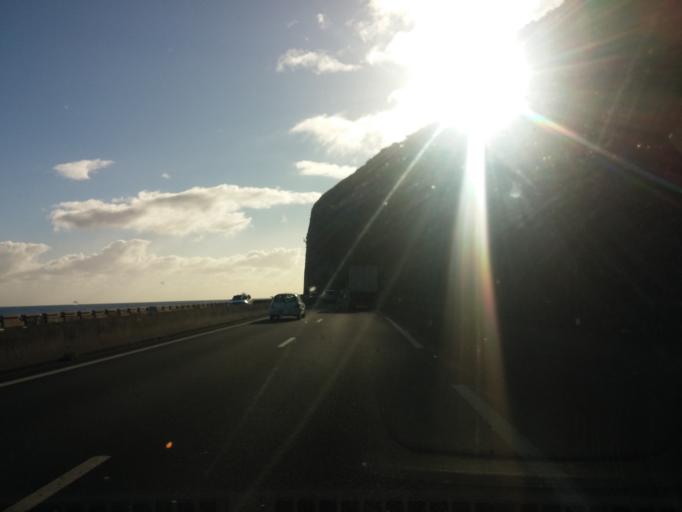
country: RE
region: Reunion
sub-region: Reunion
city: Saint-Denis
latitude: -20.8864
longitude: 55.3915
